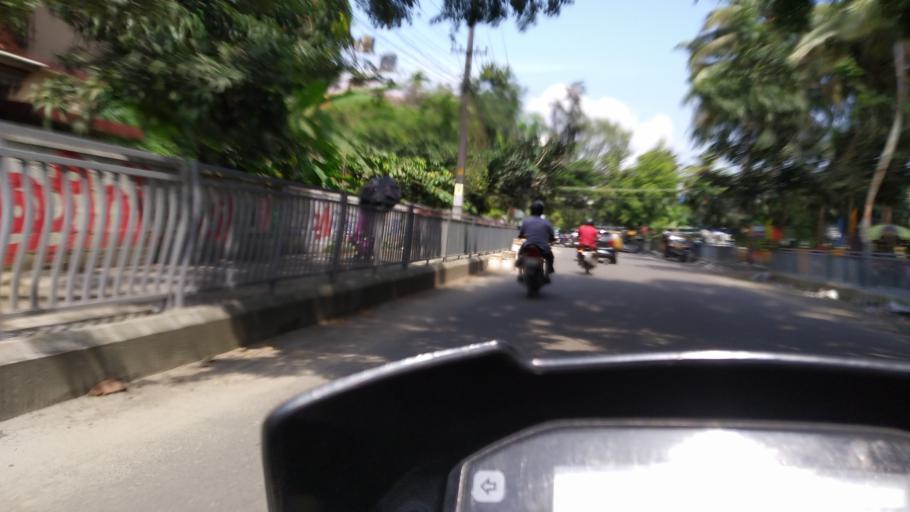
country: IN
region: Kerala
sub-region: Ernakulam
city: Cochin
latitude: 9.9714
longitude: 76.2998
